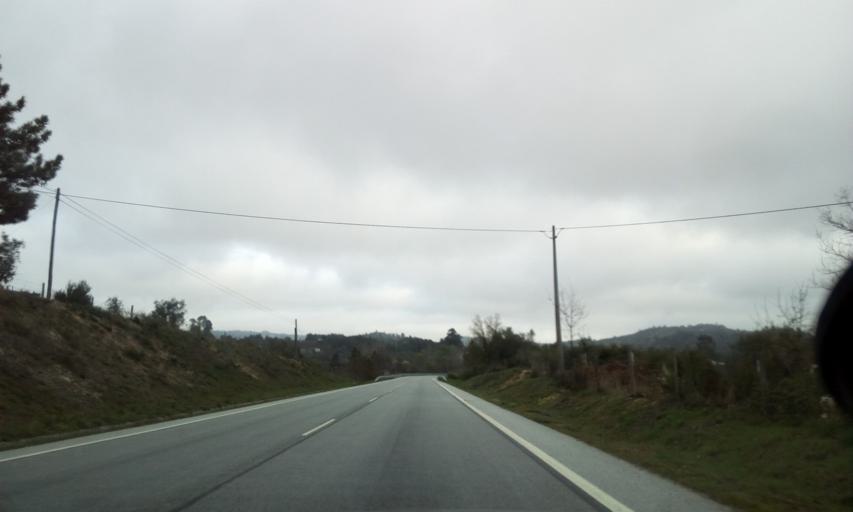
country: PT
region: Guarda
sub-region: Fornos de Algodres
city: Fornos de Algodres
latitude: 40.6318
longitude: -7.5016
